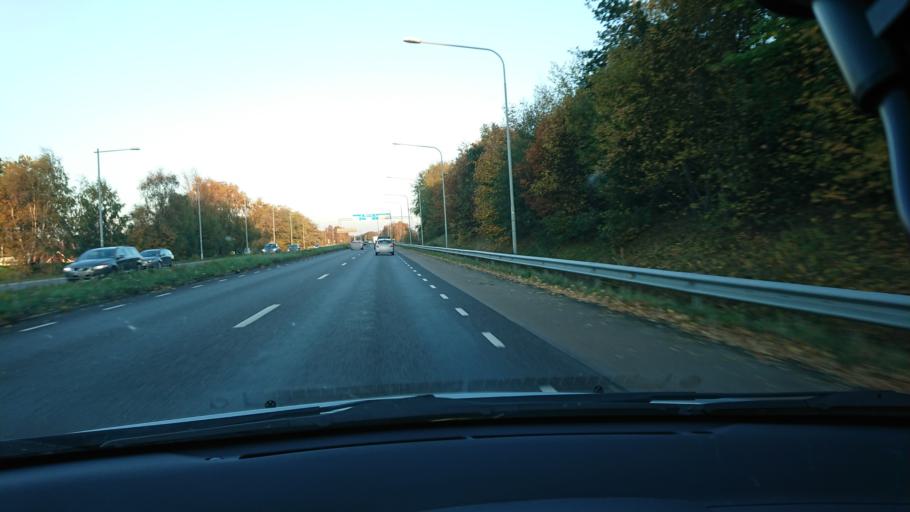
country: SE
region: Halland
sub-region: Halmstads Kommun
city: Fyllinge
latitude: 56.6748
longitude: 12.9062
